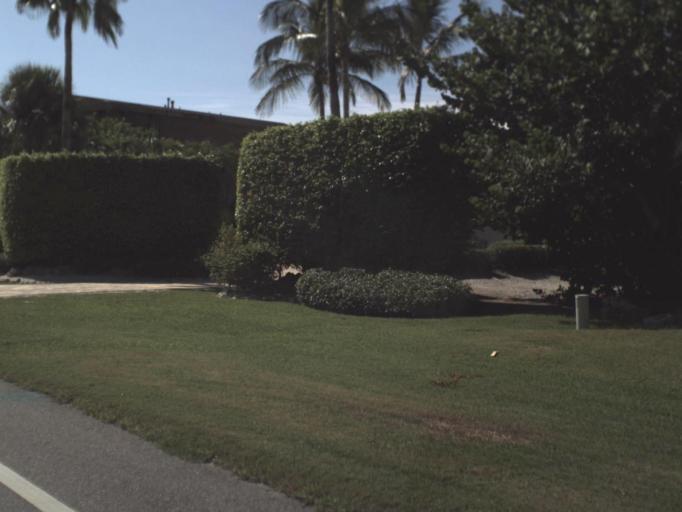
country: US
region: Florida
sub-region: Manatee County
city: Longboat Key
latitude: 27.4305
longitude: -82.6813
